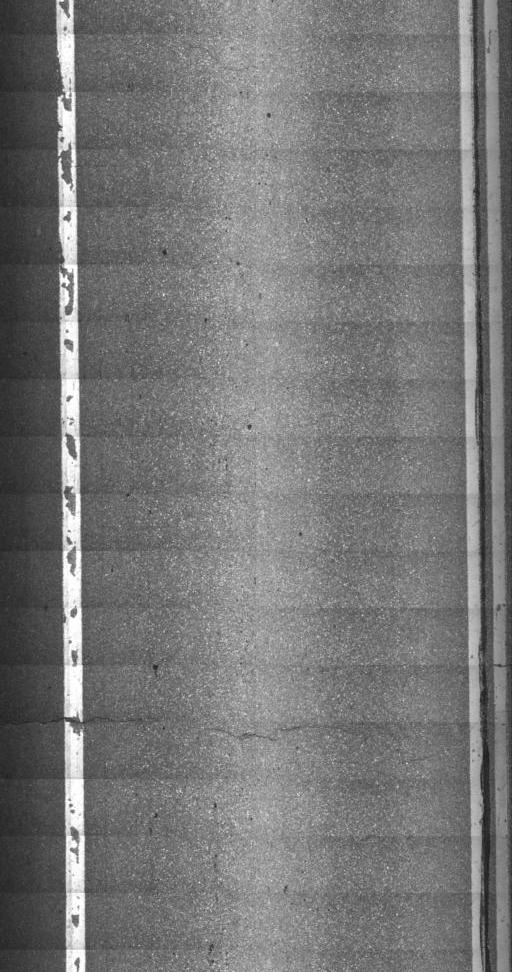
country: US
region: Vermont
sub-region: Chittenden County
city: Jericho
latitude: 44.5931
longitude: -73.0126
